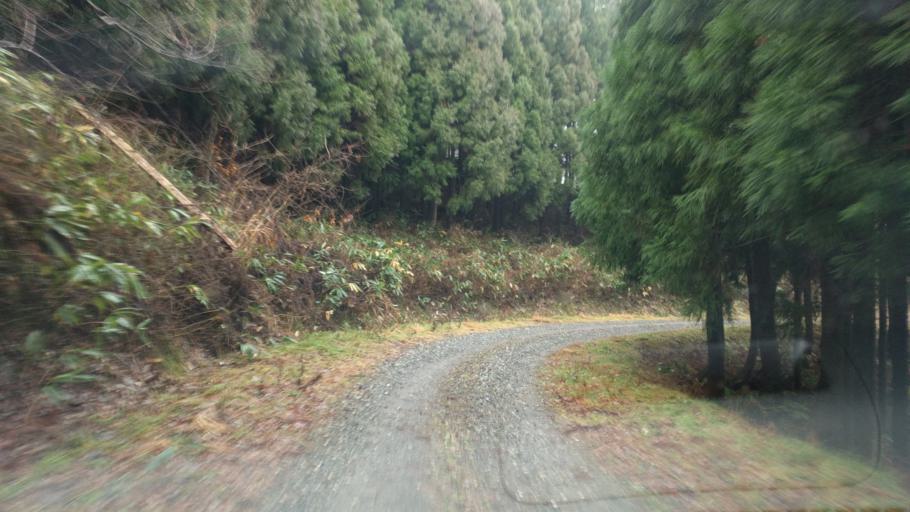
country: JP
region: Fukushima
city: Kitakata
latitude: 37.5754
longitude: 139.9788
